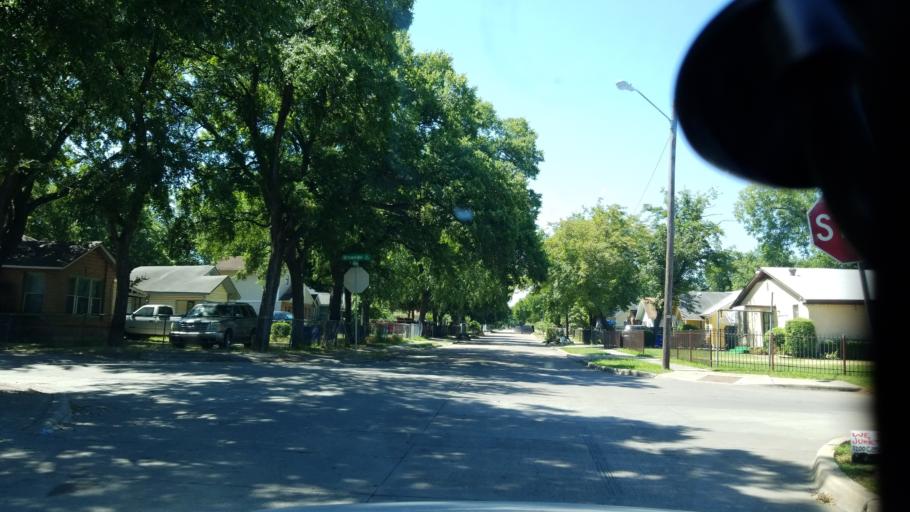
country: US
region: Texas
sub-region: Dallas County
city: Cockrell Hill
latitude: 32.7115
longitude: -96.8218
